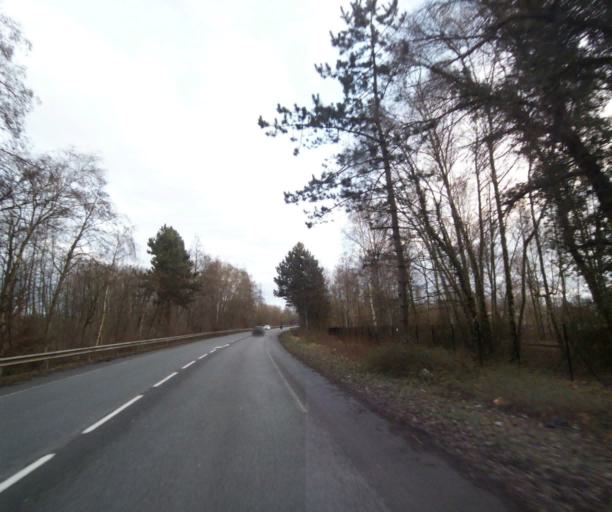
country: FR
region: Nord-Pas-de-Calais
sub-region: Departement du Nord
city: Saint-Saulve
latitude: 50.3775
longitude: 3.5411
